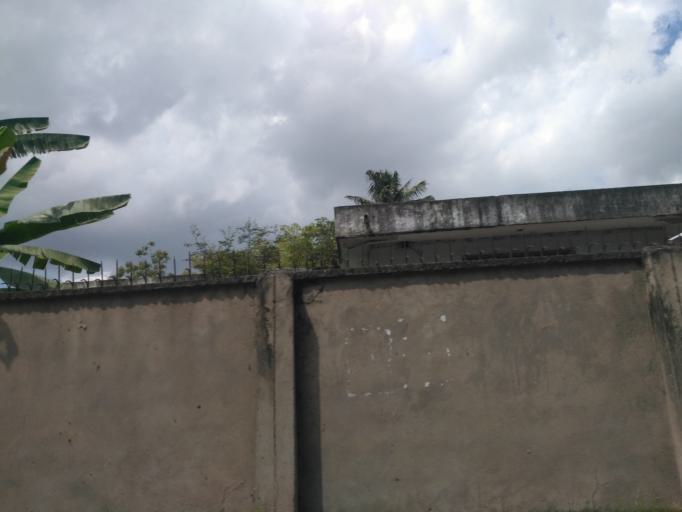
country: TZ
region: Dar es Salaam
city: Magomeni
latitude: -6.7614
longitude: 39.2478
